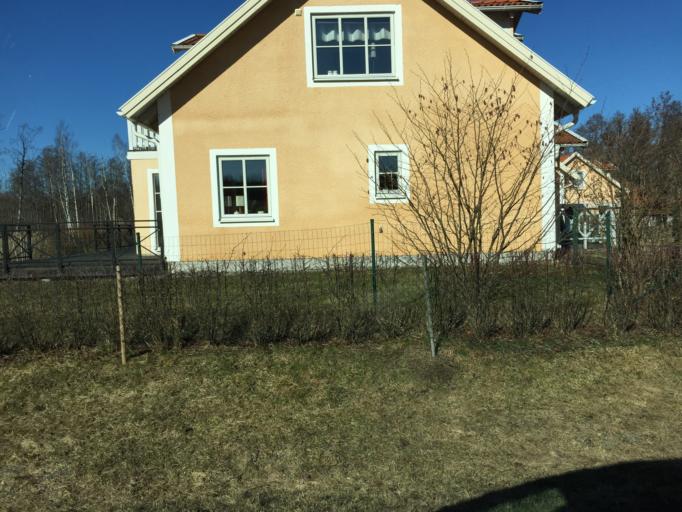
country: SE
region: OErebro
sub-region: Orebro Kommun
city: Odensbacken
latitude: 59.0131
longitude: 15.5906
